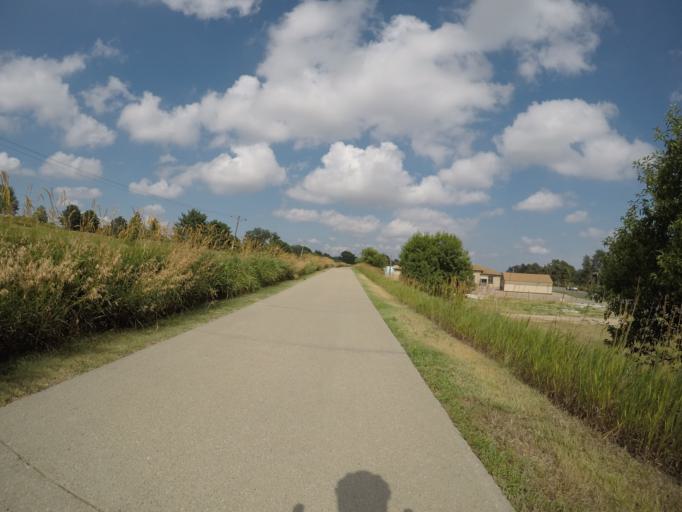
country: US
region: Nebraska
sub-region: Buffalo County
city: Kearney
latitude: 40.6998
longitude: -99.1311
